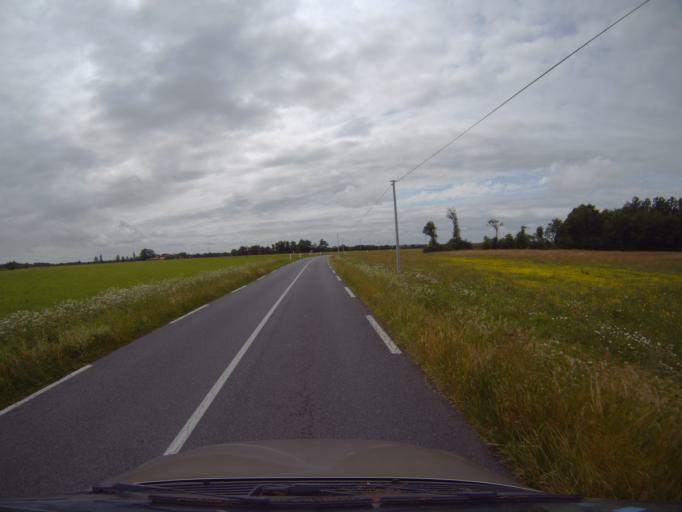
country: FR
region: Pays de la Loire
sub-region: Departement de la Loire-Atlantique
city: Aigrefeuille-sur-Maine
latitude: 47.0606
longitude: -1.4415
